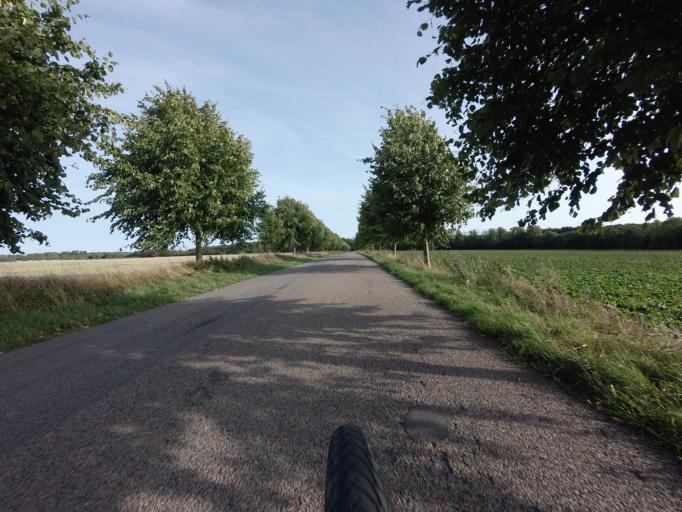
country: DK
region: Zealand
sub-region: Faxe Kommune
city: Fakse Ladeplads
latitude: 55.2472
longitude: 12.2297
